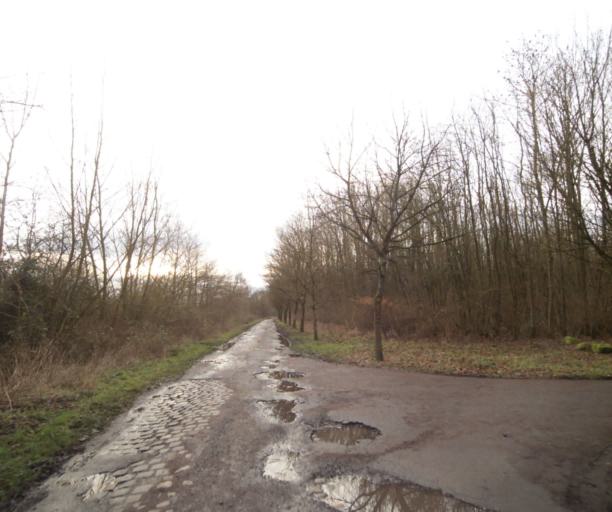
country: BE
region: Wallonia
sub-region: Province du Hainaut
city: Bernissart
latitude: 50.4698
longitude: 3.6177
